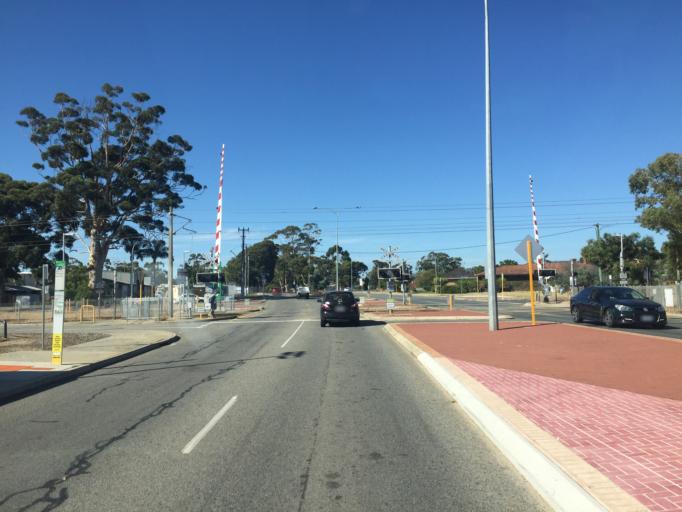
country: AU
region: Western Australia
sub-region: Gosnells
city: Maddington
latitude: -32.0506
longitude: 115.9843
